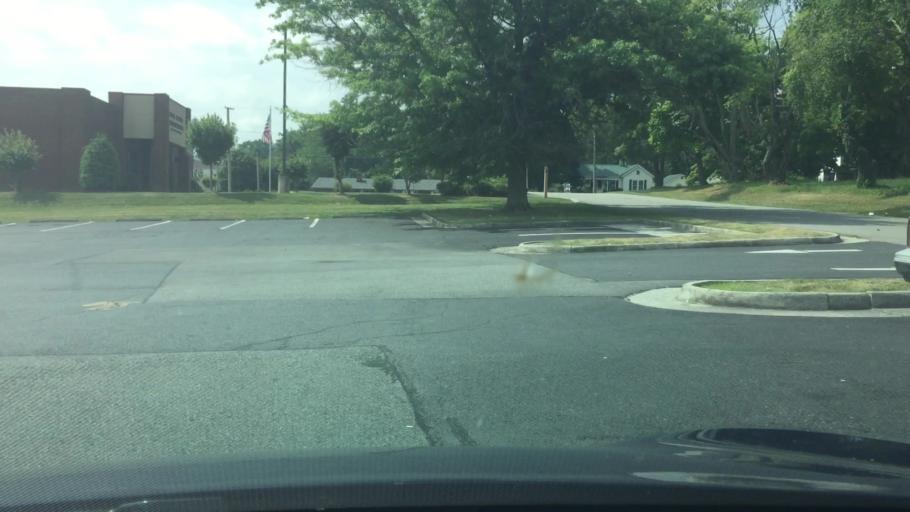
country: US
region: Virginia
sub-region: Wythe County
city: Wytheville
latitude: 36.9519
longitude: -81.0731
